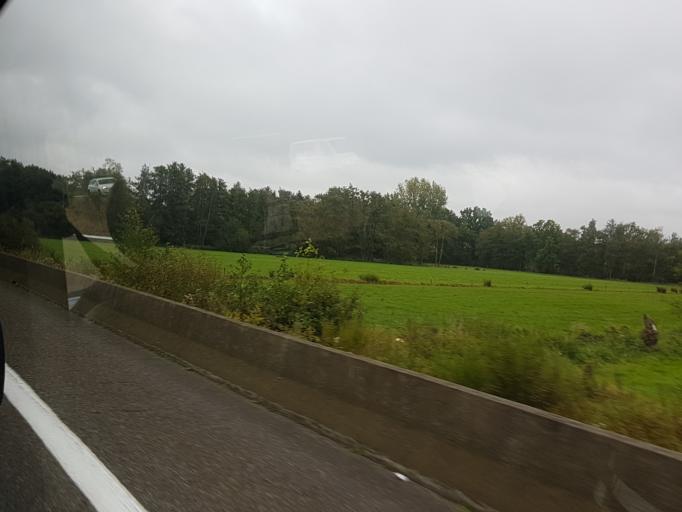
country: BE
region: Flanders
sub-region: Provincie Antwerpen
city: Meerhout
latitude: 51.1707
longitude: 5.0663
